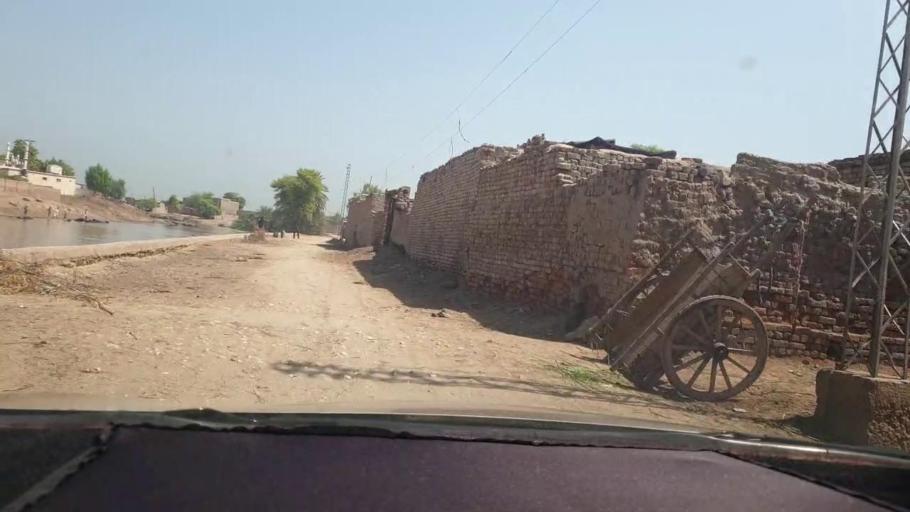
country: PK
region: Sindh
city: Kambar
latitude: 27.5886
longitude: 68.0618
